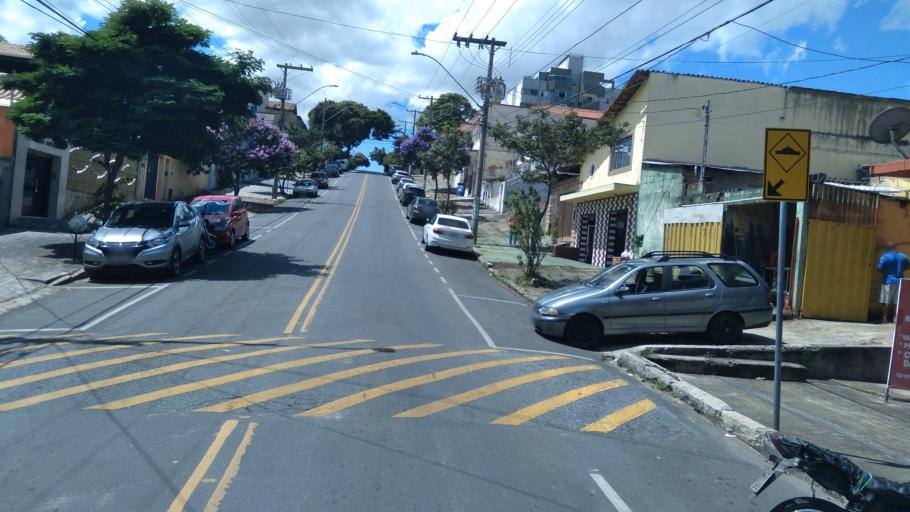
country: BR
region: Minas Gerais
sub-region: Belo Horizonte
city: Belo Horizonte
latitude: -19.8854
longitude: -43.9092
